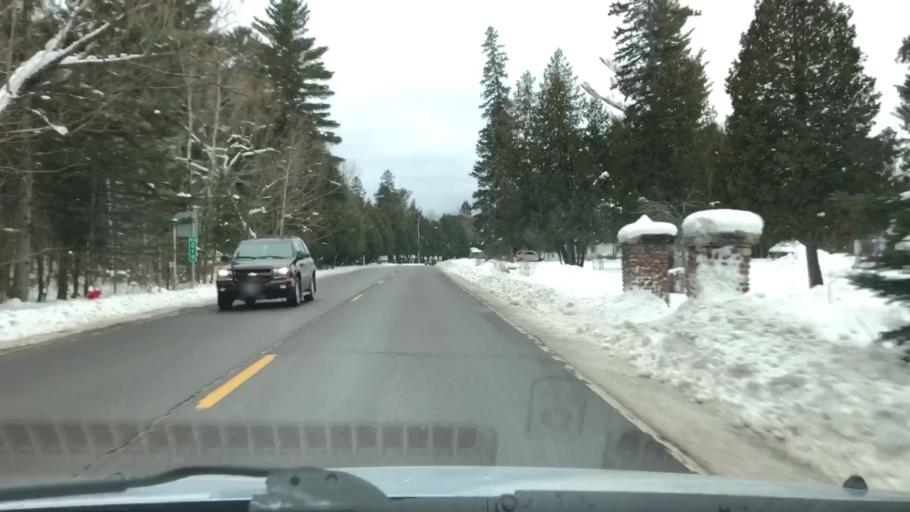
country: US
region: Minnesota
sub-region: Carlton County
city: Carlton
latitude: 46.6645
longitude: -92.4166
